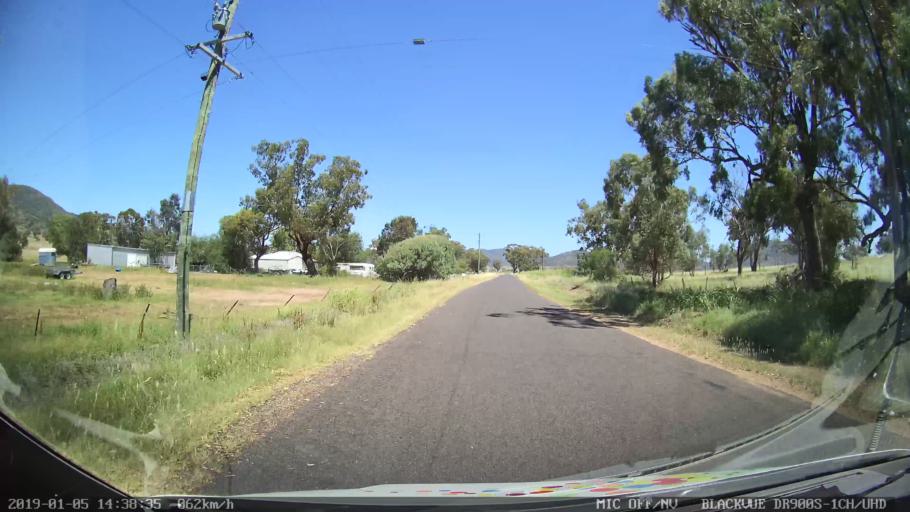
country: AU
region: New South Wales
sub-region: Tamworth Municipality
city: Phillip
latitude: -31.2499
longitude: 150.6926
